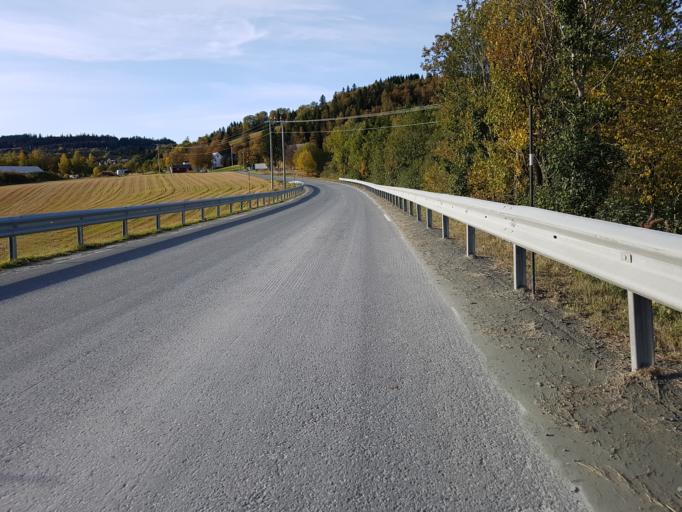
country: NO
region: Sor-Trondelag
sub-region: Klaebu
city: Klaebu
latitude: 63.3487
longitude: 10.5018
